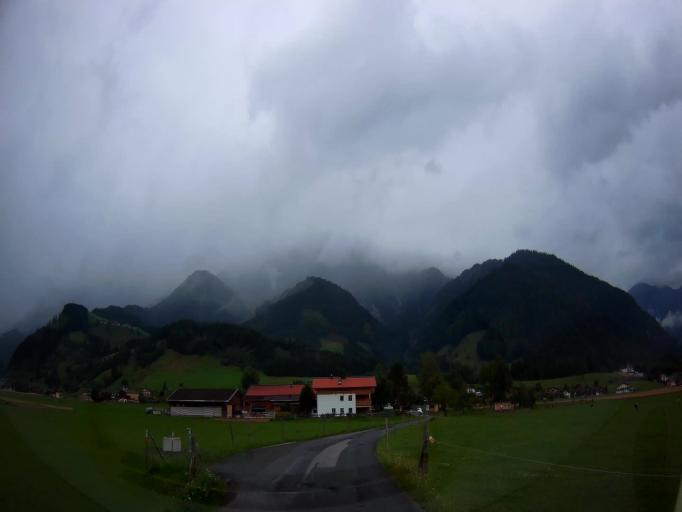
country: AT
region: Salzburg
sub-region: Politischer Bezirk Zell am See
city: Leogang
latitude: 47.4415
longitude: 12.7965
